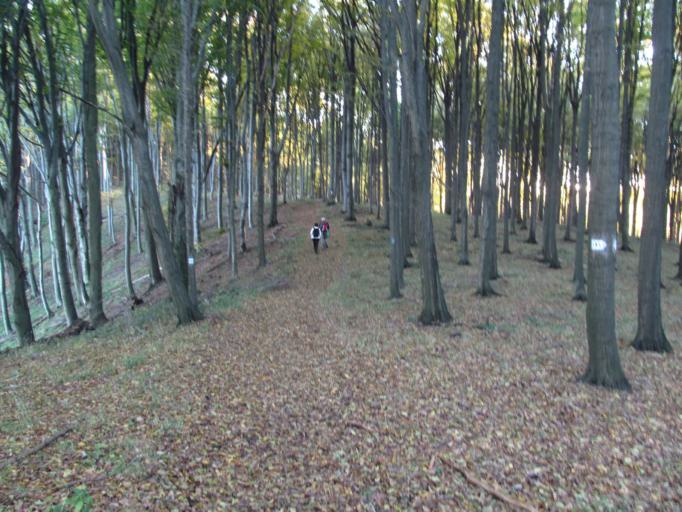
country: HU
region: Heves
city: Paradsasvar
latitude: 47.8972
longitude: 19.9664
